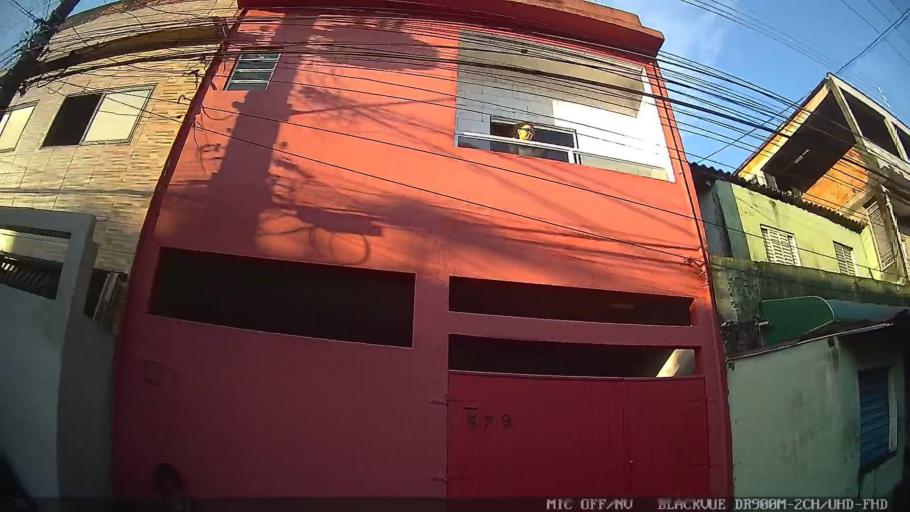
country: BR
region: Sao Paulo
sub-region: Guaruja
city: Guaruja
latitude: -23.9866
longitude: -46.2758
